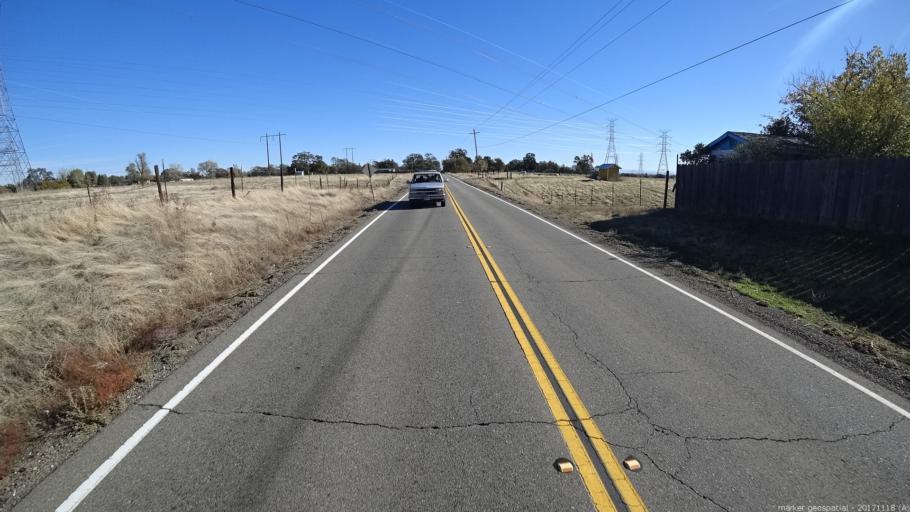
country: US
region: California
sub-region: Shasta County
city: Cottonwood
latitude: 40.3887
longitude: -122.3867
